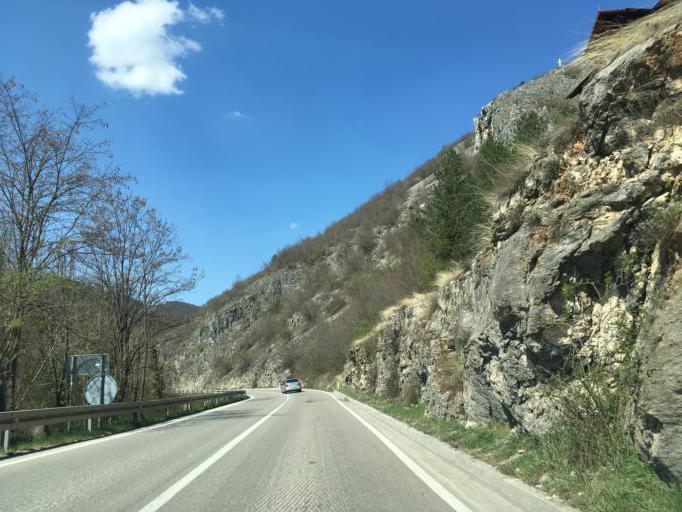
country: BA
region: Federation of Bosnia and Herzegovina
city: Divicani
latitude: 44.3701
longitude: 17.2999
